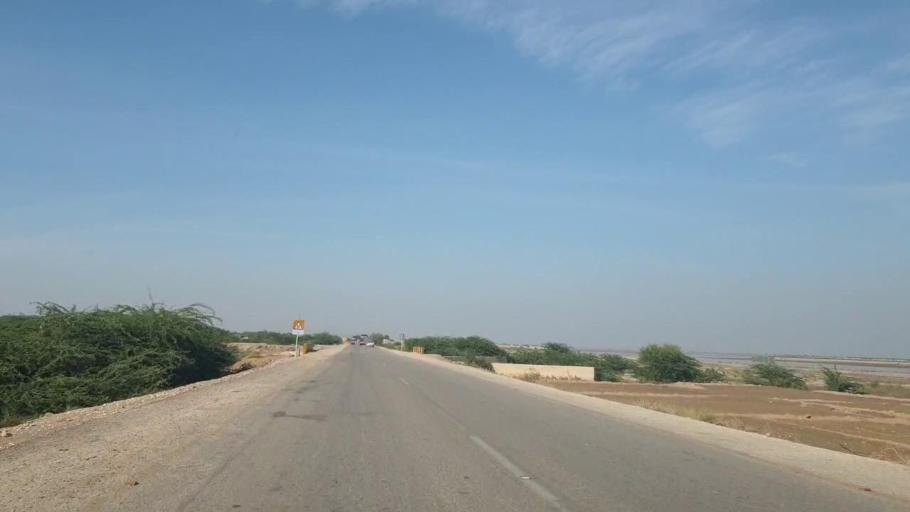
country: PK
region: Sindh
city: Sehwan
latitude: 26.3789
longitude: 67.8725
